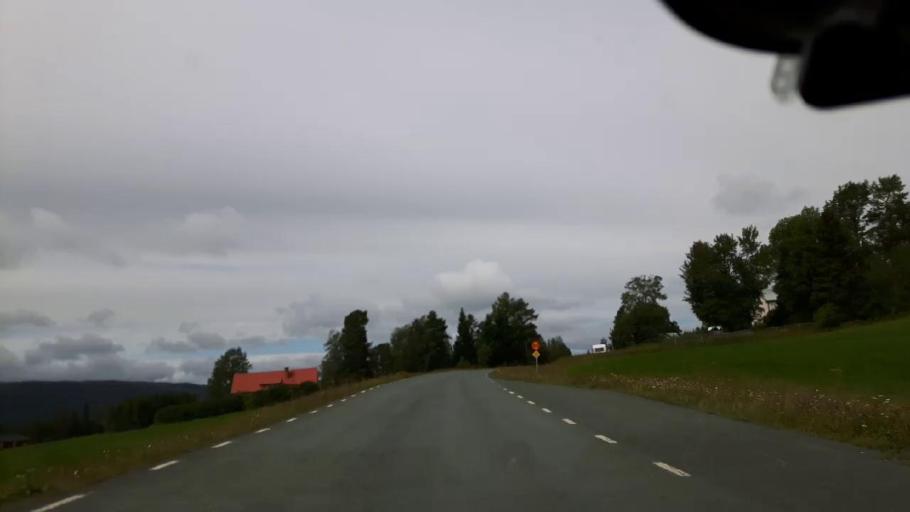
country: SE
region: Jaemtland
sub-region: Krokoms Kommun
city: Valla
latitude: 63.4538
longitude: 14.0479
